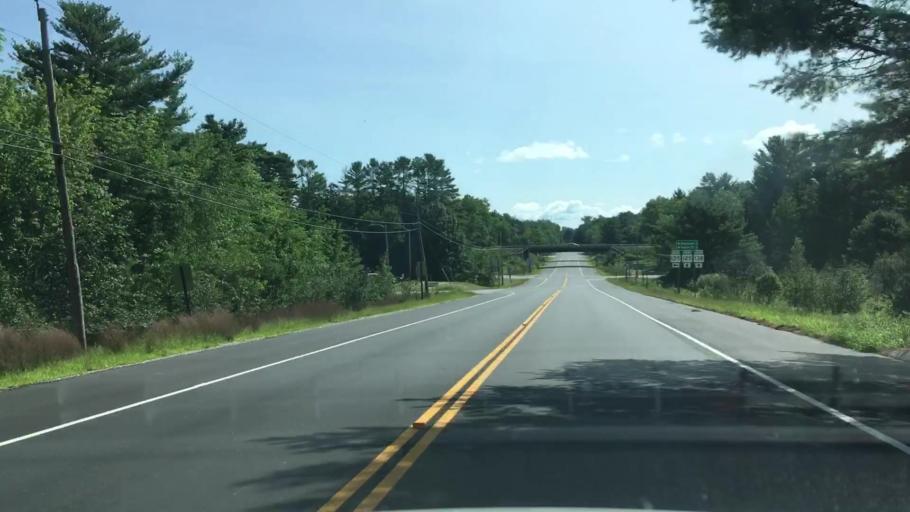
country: US
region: Maine
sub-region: Sagadahoc County
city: Topsham
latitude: 44.0178
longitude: -69.9240
